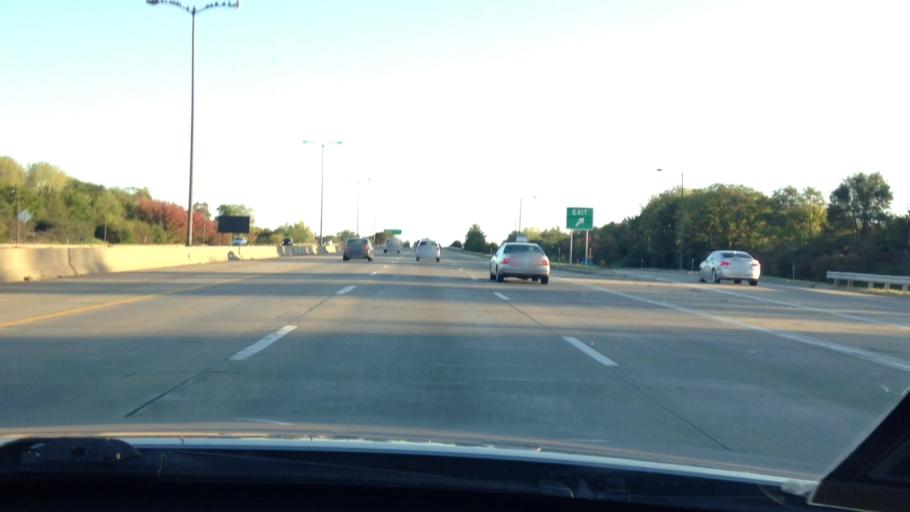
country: US
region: Missouri
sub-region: Jackson County
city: Kansas City
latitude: 39.0769
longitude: -94.5624
